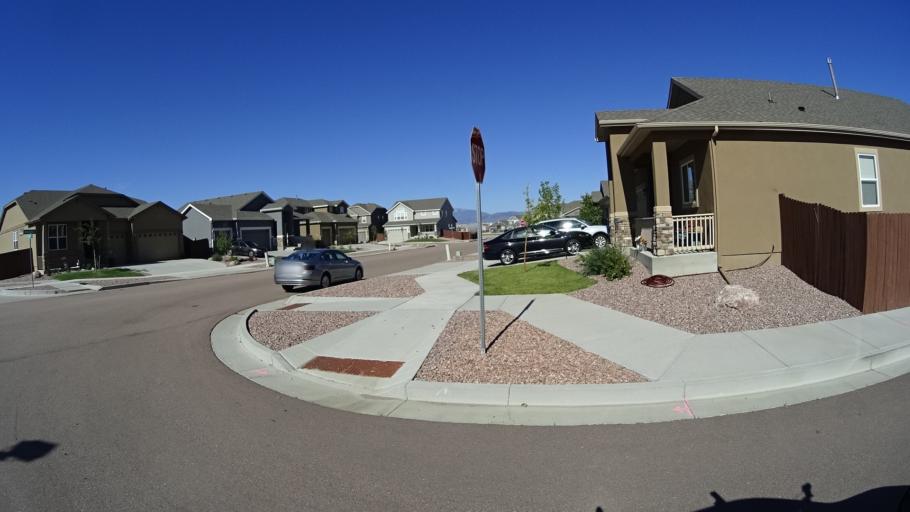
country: US
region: Colorado
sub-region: El Paso County
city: Black Forest
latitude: 38.9485
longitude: -104.6738
